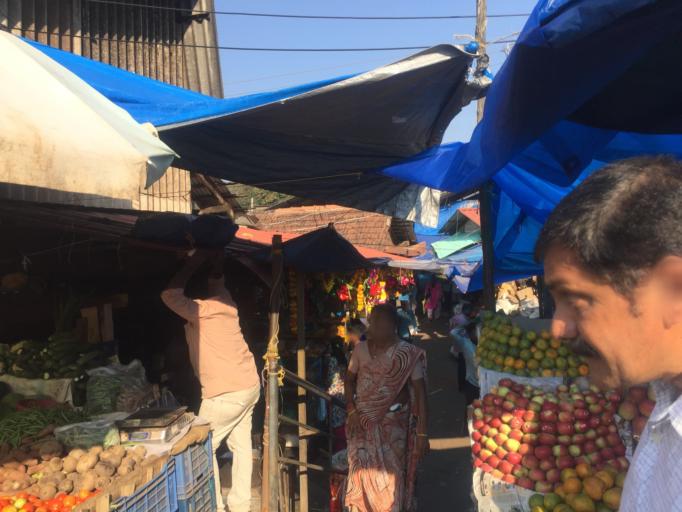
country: IN
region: Karnataka
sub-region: Dakshina Kannada
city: Mangalore
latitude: 12.8629
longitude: 74.8367
